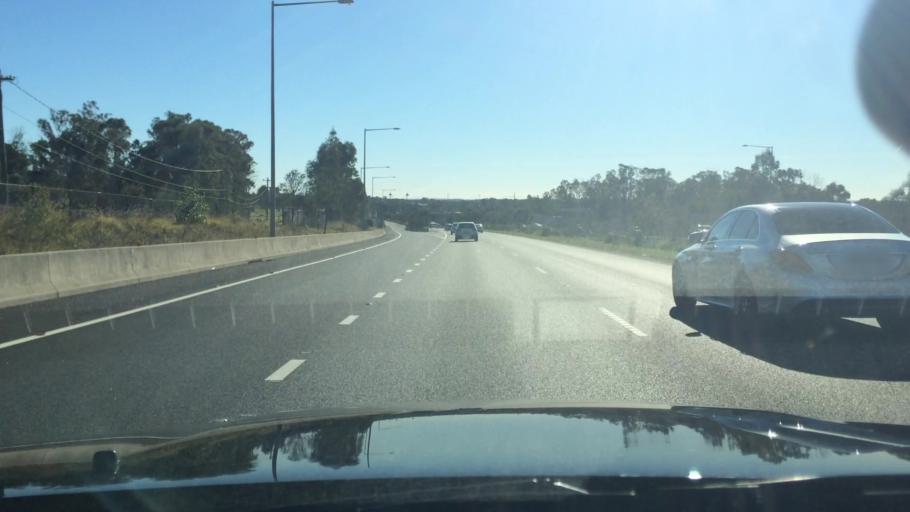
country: AU
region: New South Wales
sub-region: Fairfield
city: Horsley Park
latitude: -33.8472
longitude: 150.8535
